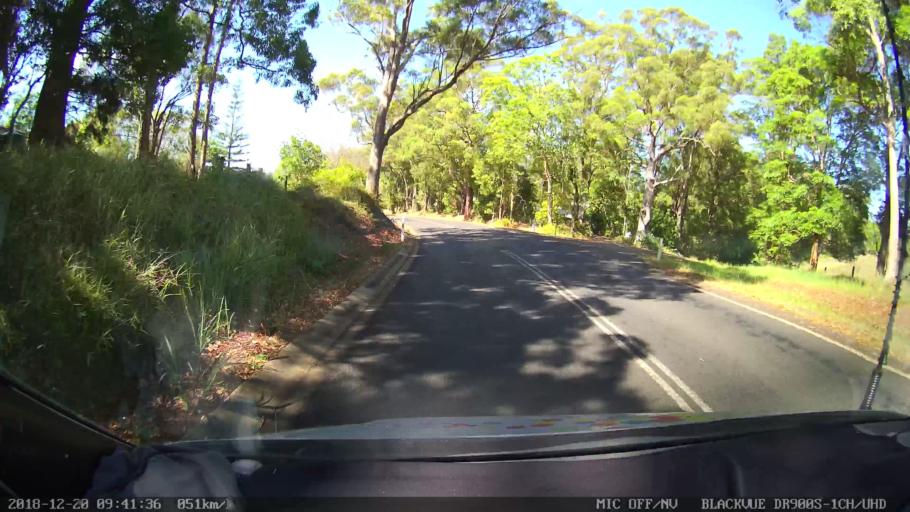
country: AU
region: New South Wales
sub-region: Lismore Municipality
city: Lismore
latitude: -28.7101
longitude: 153.2993
